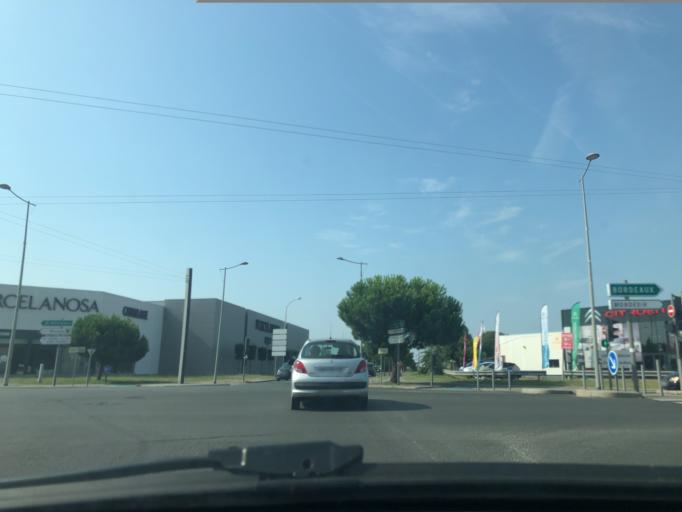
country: FR
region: Aquitaine
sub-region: Departement de la Gironde
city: Merignac
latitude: 44.8324
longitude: -0.6401
